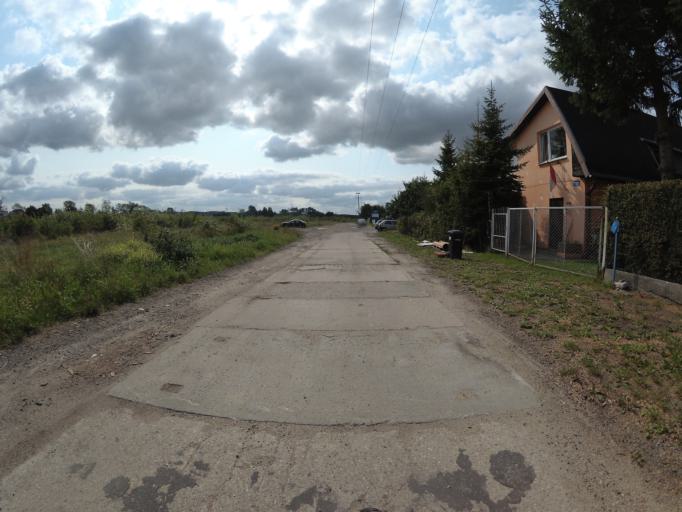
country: PL
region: Pomeranian Voivodeship
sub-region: Powiat wejherowski
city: Bojano
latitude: 54.5000
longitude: 18.4285
